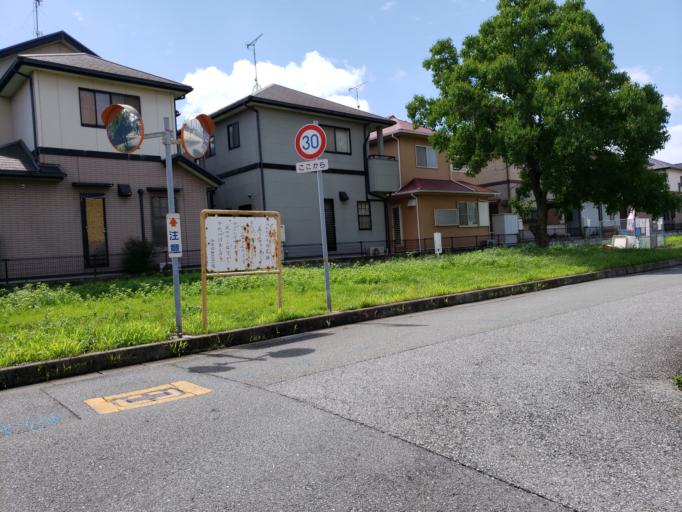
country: JP
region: Hyogo
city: Kakogawacho-honmachi
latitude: 34.7342
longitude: 134.8370
